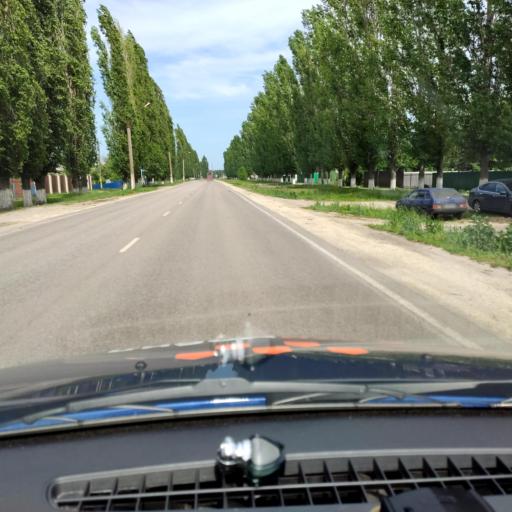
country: RU
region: Voronezj
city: Maslovka
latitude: 51.5422
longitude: 39.3485
